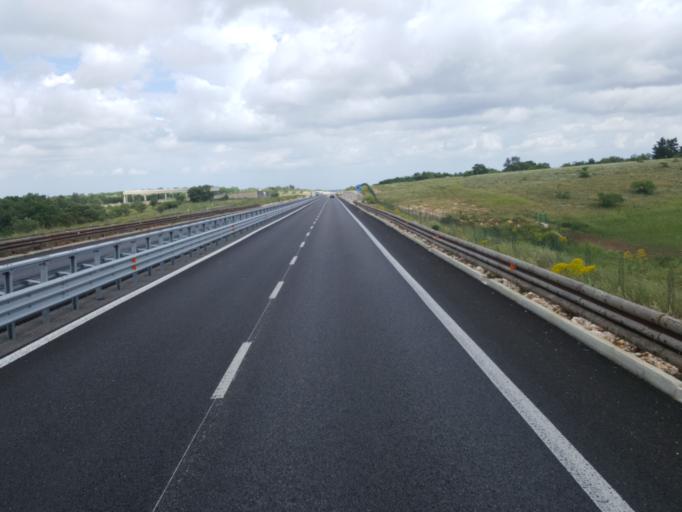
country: IT
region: Apulia
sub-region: Provincia di Bari
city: Quasano
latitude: 40.9054
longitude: 16.6270
